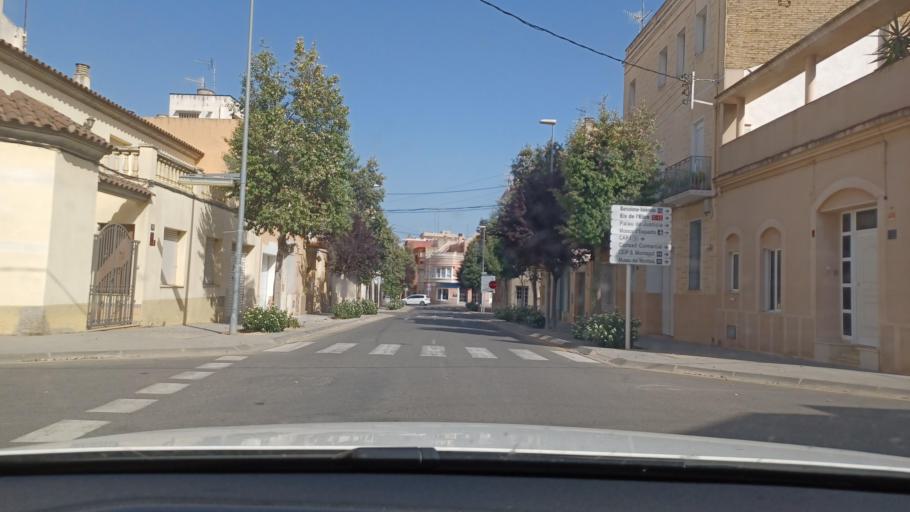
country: ES
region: Catalonia
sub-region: Provincia de Tarragona
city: Amposta
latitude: 40.7115
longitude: 0.5759
